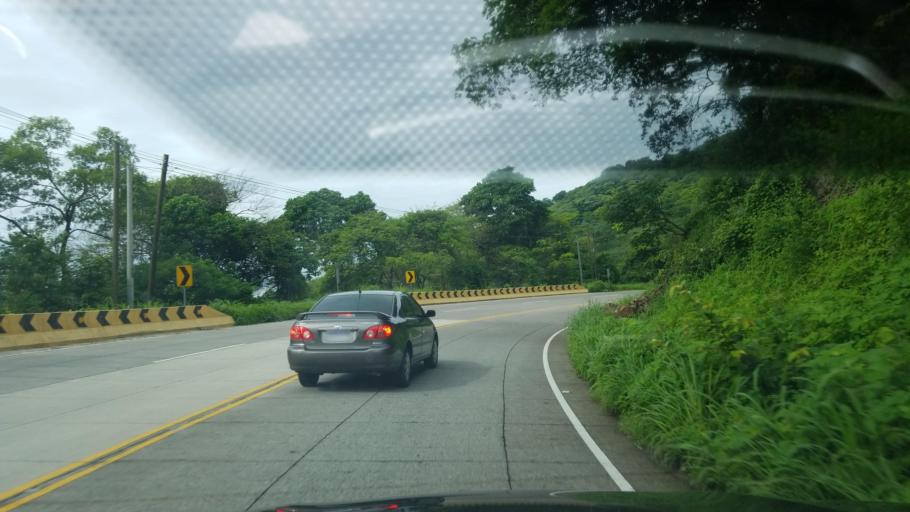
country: HN
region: Francisco Morazan
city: El Porvenir
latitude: 13.7134
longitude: -87.3169
